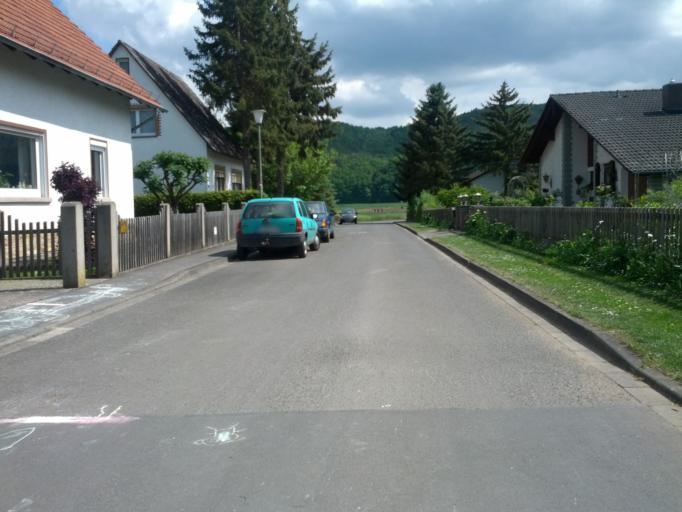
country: DE
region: Thuringia
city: Treffurt
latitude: 51.1278
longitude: 10.2005
